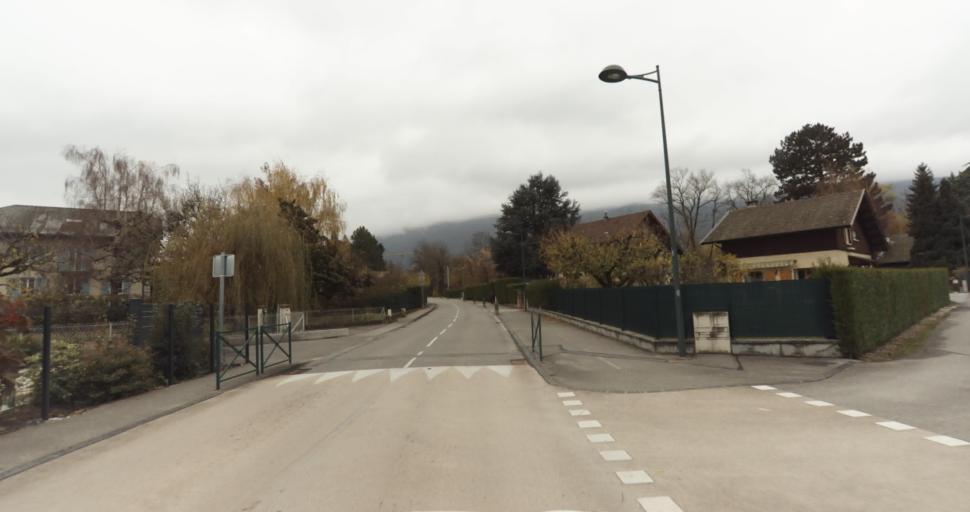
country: FR
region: Rhone-Alpes
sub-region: Departement de la Haute-Savoie
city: Saint-Jorioz
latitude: 45.8365
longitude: 6.1690
